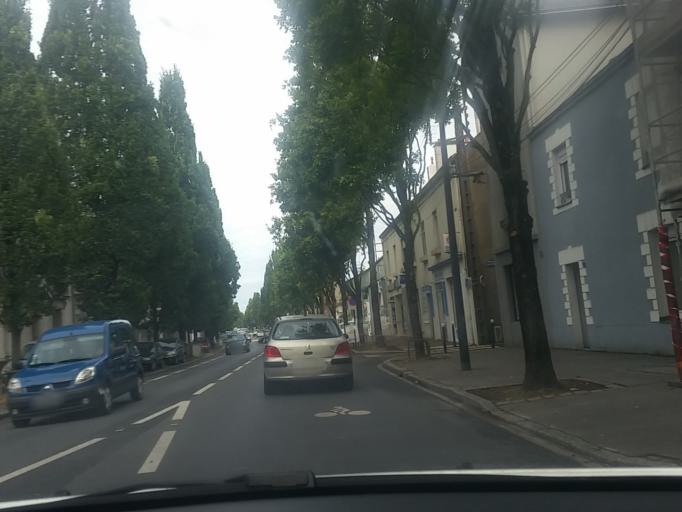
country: FR
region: Pays de la Loire
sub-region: Departement de la Loire-Atlantique
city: Nantes
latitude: 47.2366
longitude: -1.5686
